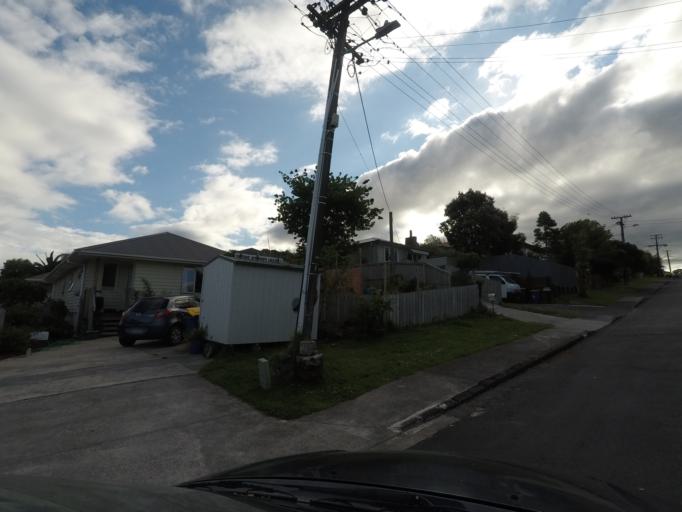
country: NZ
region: Auckland
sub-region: Auckland
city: Rosebank
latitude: -36.8844
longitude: 174.6531
